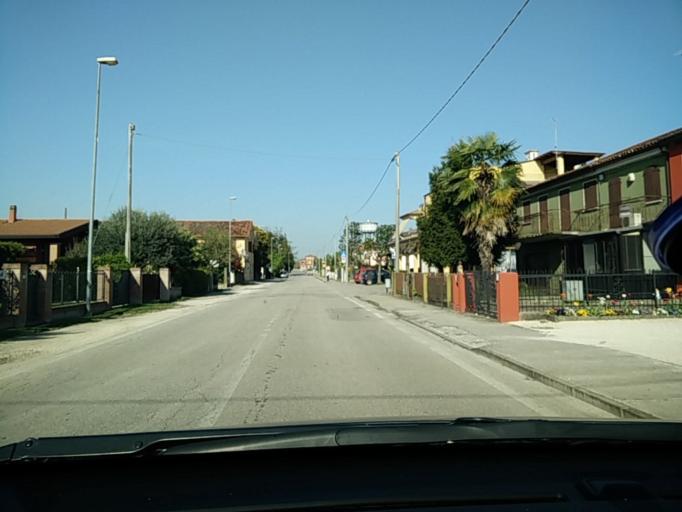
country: IT
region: Veneto
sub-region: Provincia di Venezia
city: Fossalta di Piave
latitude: 45.6326
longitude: 12.5209
